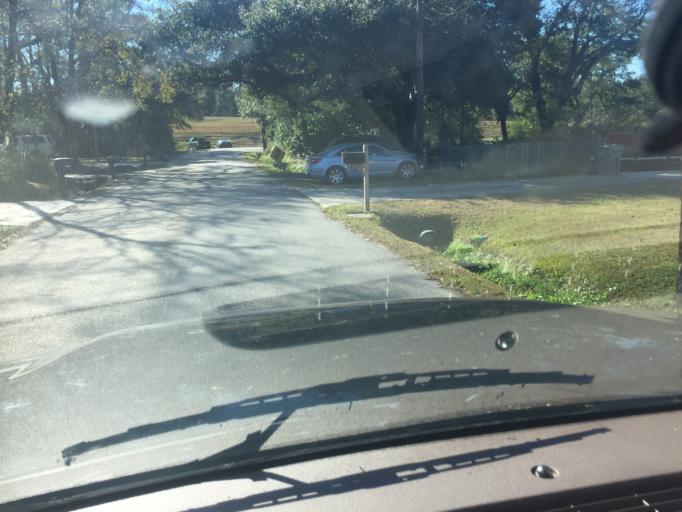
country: US
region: Louisiana
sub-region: Saint Tammany Parish
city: Slidell
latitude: 30.3115
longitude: -89.7411
